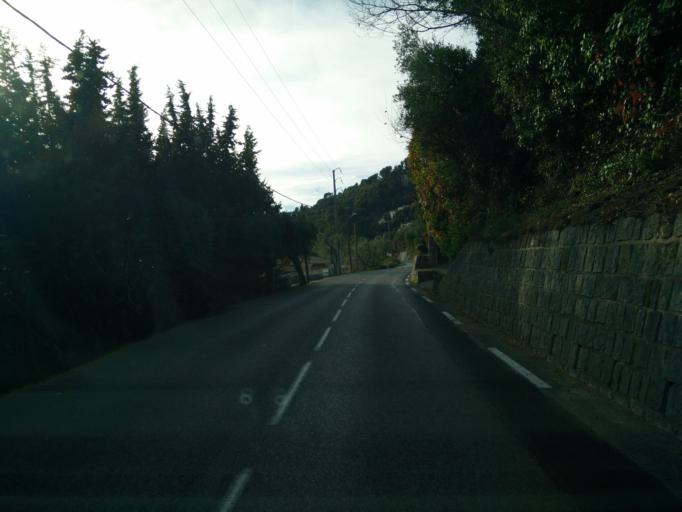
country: FR
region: Provence-Alpes-Cote d'Azur
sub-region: Departement des Alpes-Maritimes
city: Le Tignet
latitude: 43.6385
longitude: 6.8407
